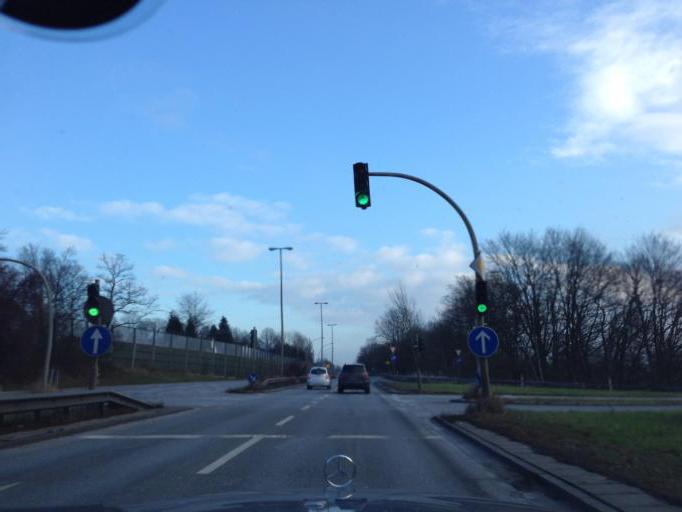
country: DE
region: Schleswig-Holstein
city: Oststeinbek
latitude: 53.5270
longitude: 10.1343
